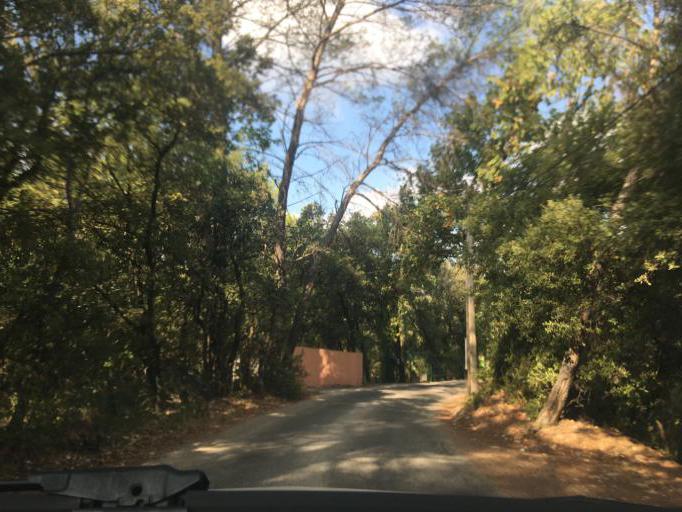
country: FR
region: Provence-Alpes-Cote d'Azur
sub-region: Departement du Var
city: Lorgues
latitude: 43.4933
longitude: 6.3941
